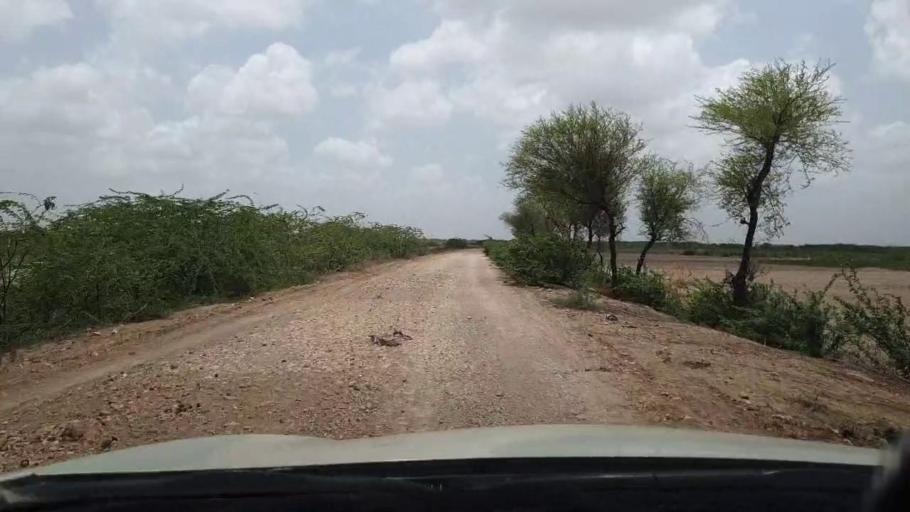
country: PK
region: Sindh
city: Kadhan
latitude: 24.3883
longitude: 68.9337
